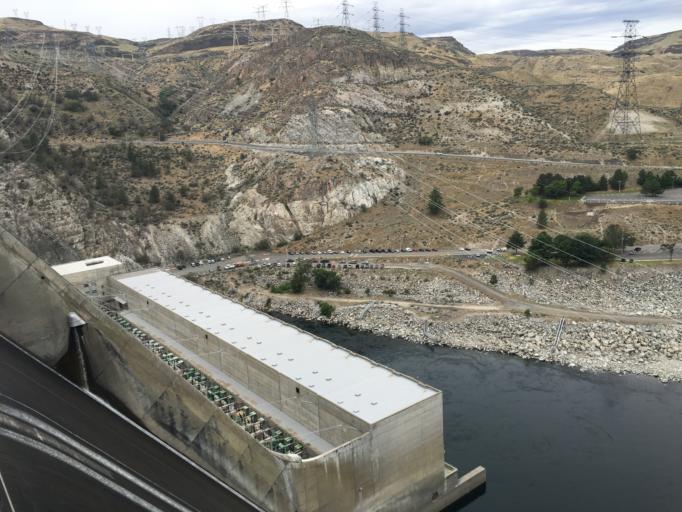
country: US
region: Washington
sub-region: Okanogan County
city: Coulee Dam
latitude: 47.9558
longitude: -118.9839
